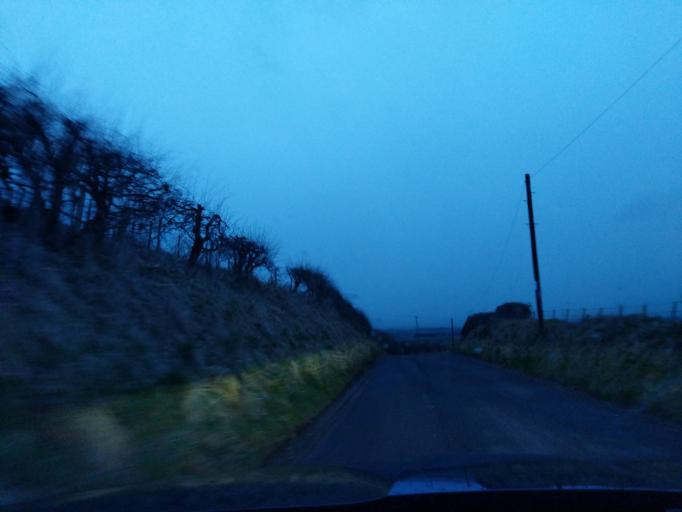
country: GB
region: England
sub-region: Northumberland
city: Ford
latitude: 55.7118
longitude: -2.1022
